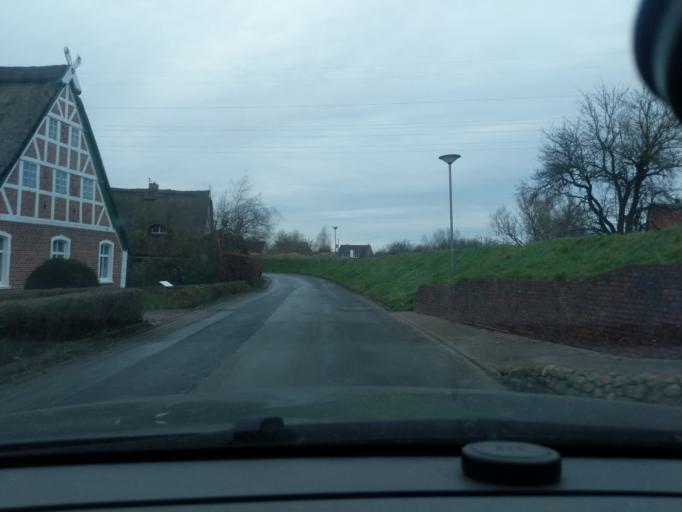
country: DE
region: Lower Saxony
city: Mittelnkirchen
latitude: 53.5361
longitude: 9.6124
